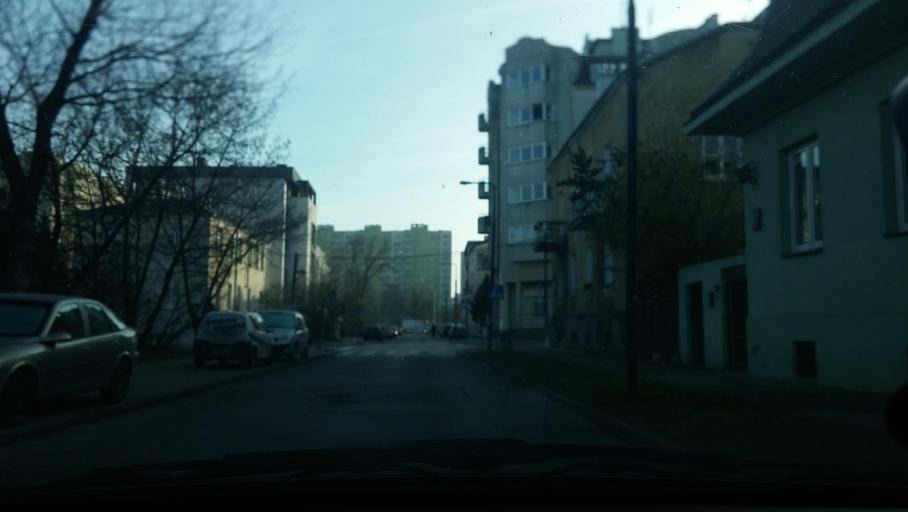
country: PL
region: Masovian Voivodeship
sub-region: Warszawa
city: Praga Poludnie
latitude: 52.2387
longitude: 21.1044
